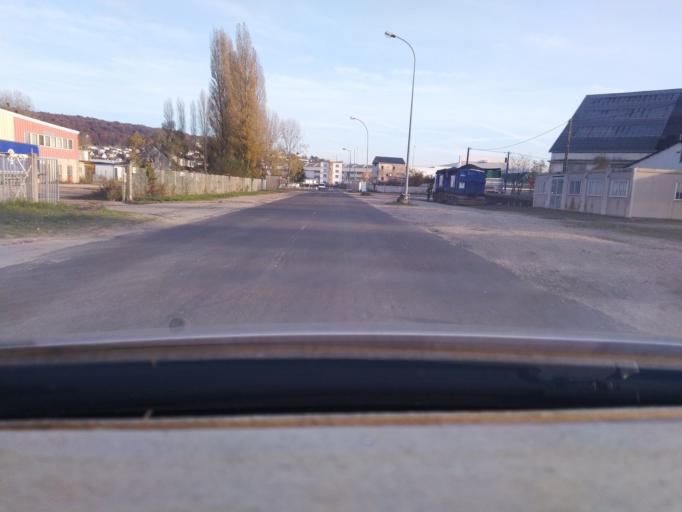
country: FR
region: Haute-Normandie
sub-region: Departement de la Seine-Maritime
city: Le Trait
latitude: 49.4824
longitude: 0.7984
